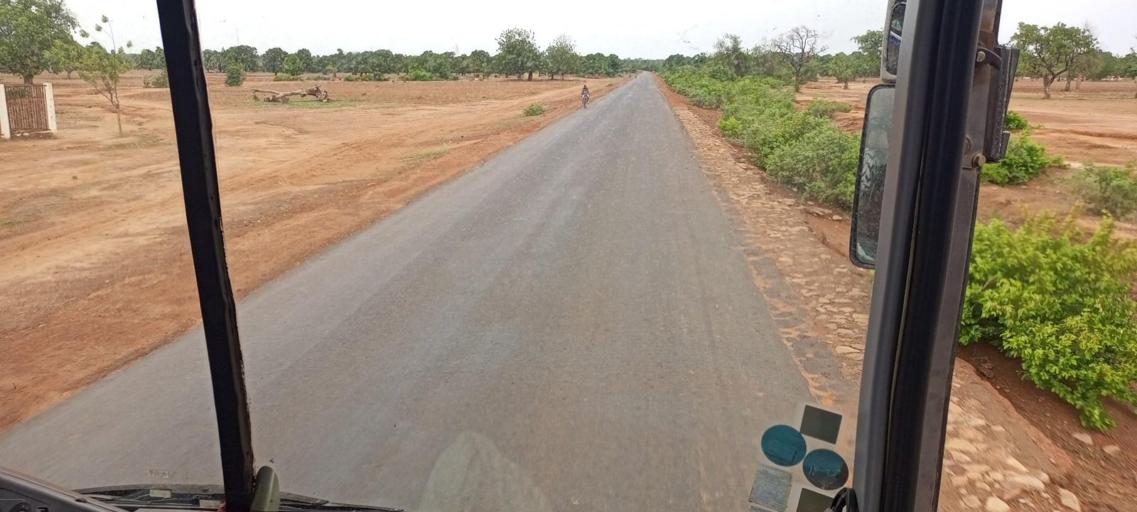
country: ML
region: Segou
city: Bla
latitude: 12.6859
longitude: -5.7236
